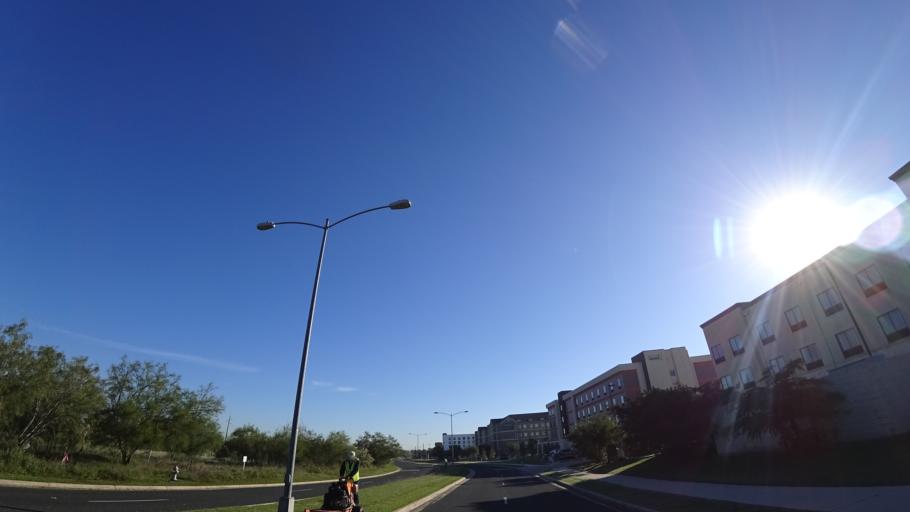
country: US
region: Texas
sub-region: Travis County
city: Austin
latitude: 30.2207
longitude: -97.6916
